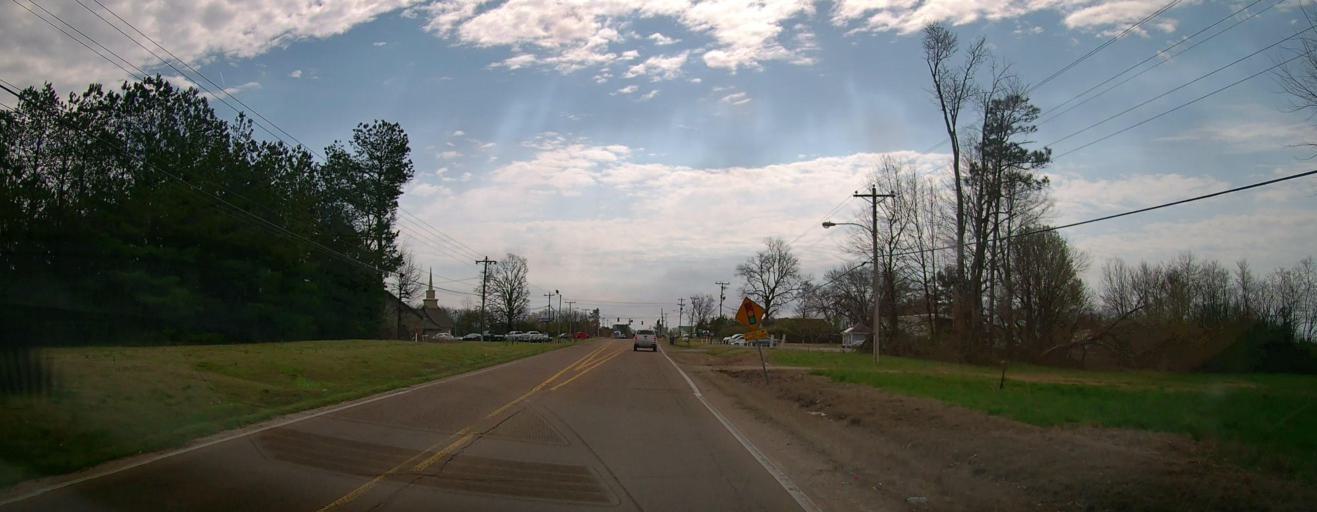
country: US
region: Mississippi
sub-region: De Soto County
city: Olive Branch
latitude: 34.9342
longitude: -89.7970
